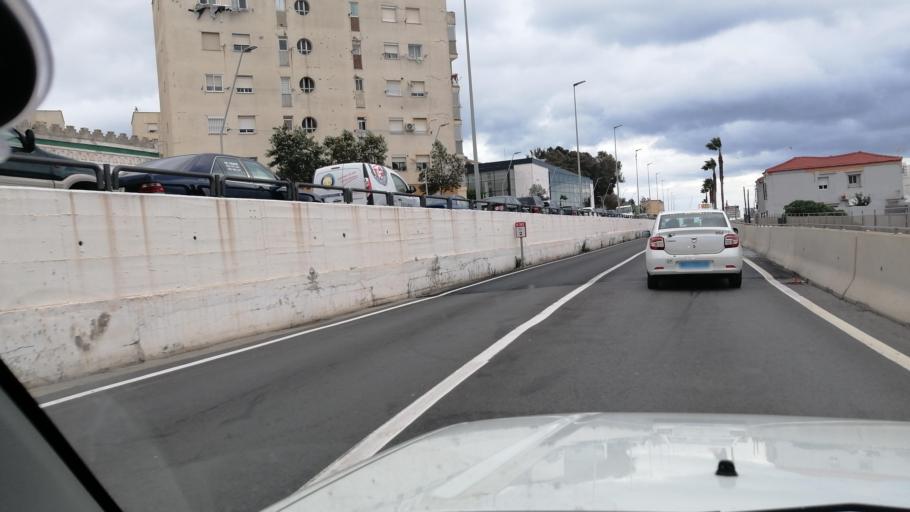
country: ES
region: Ceuta
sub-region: Ceuta
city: Ceuta
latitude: 35.8800
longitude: -5.3335
